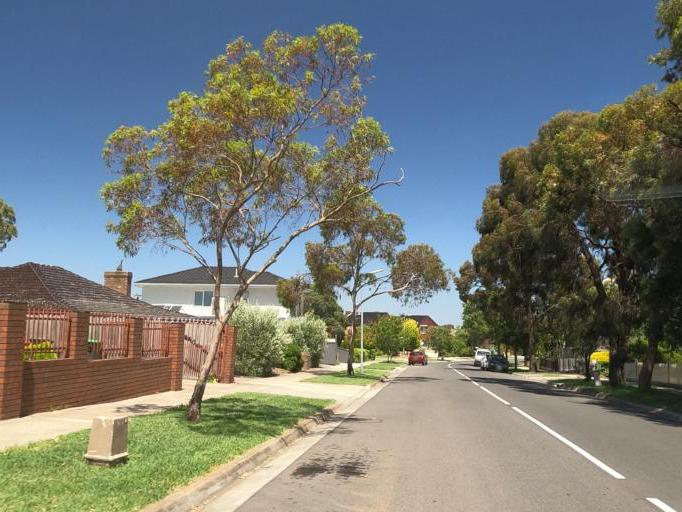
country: AU
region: Victoria
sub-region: Hume
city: Greenvale
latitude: -37.6384
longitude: 144.8832
